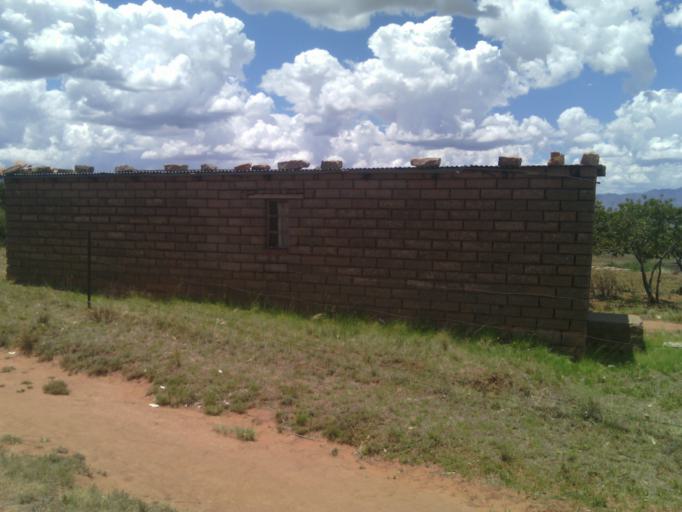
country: LS
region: Quthing
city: Quthing
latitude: -30.3827
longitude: 27.5583
